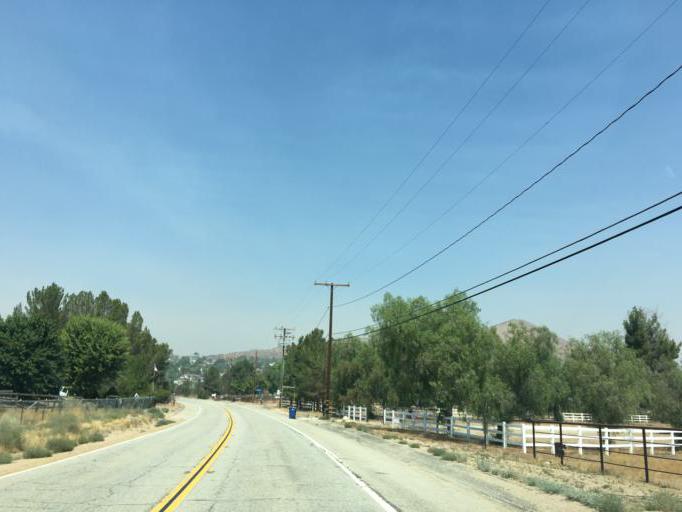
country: US
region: California
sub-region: Los Angeles County
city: Acton
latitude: 34.4741
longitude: -118.1659
